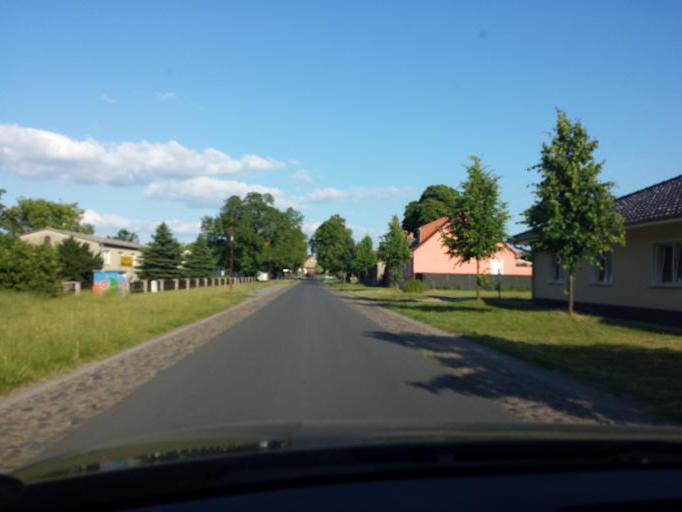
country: DE
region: Brandenburg
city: Kremmen
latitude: 52.8137
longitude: 13.0049
